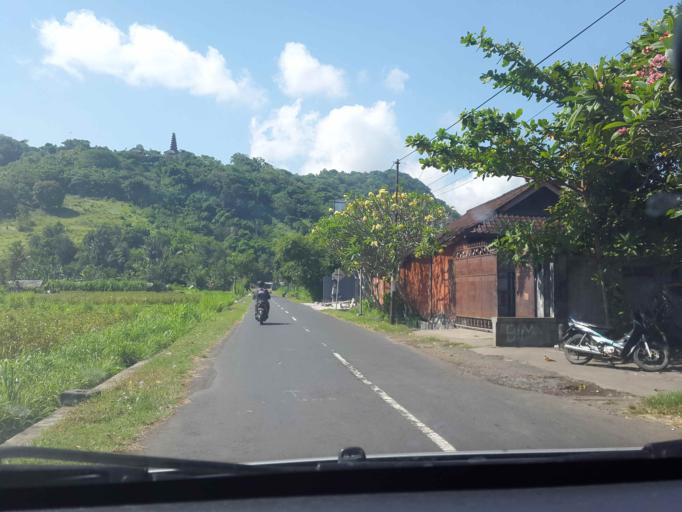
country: ID
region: Bali
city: Dawan
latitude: -8.5537
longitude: 115.4327
